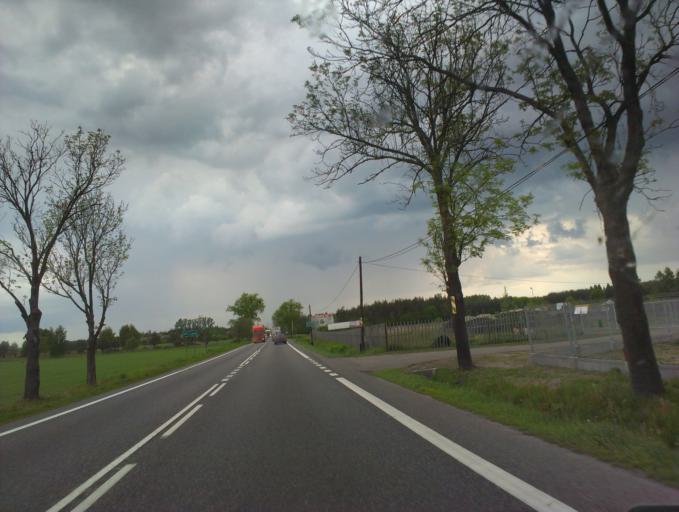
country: PL
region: Masovian Voivodeship
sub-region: Powiat zyrardowski
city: Radziejowice
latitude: 51.9348
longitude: 20.6275
